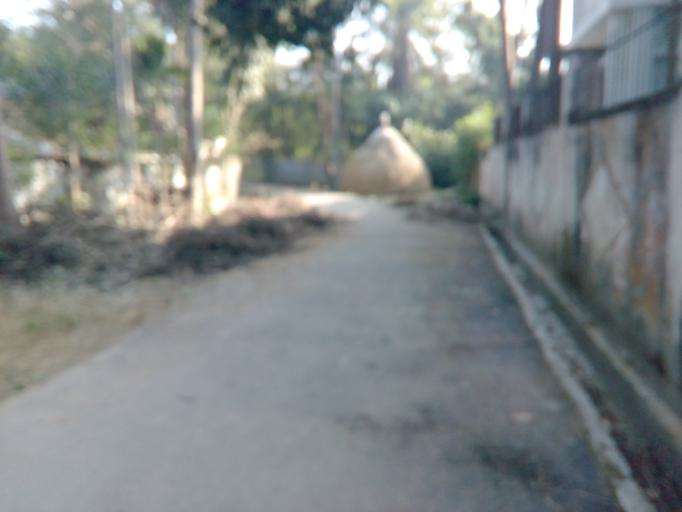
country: IN
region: Tripura
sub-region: West Tripura
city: Sonamura
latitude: 23.3210
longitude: 91.2757
